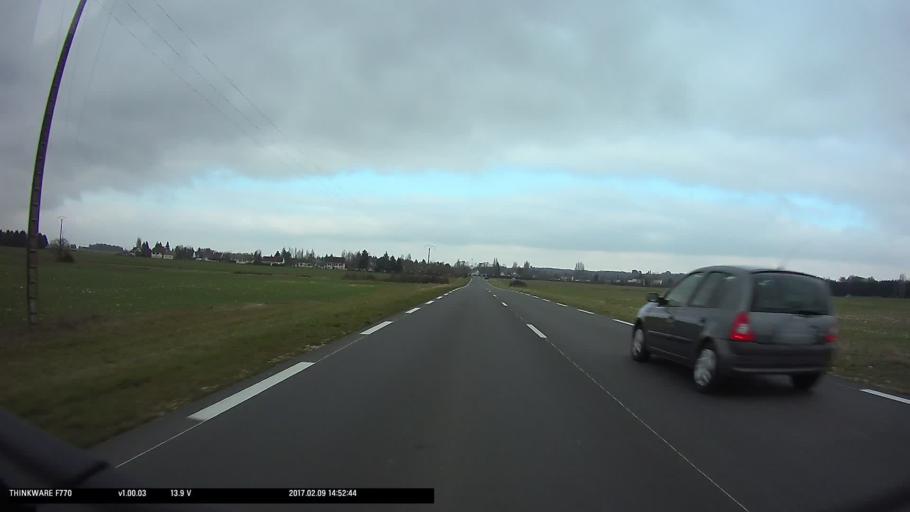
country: FR
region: Centre
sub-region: Departement du Cher
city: Levet
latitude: 46.9160
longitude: 2.4115
